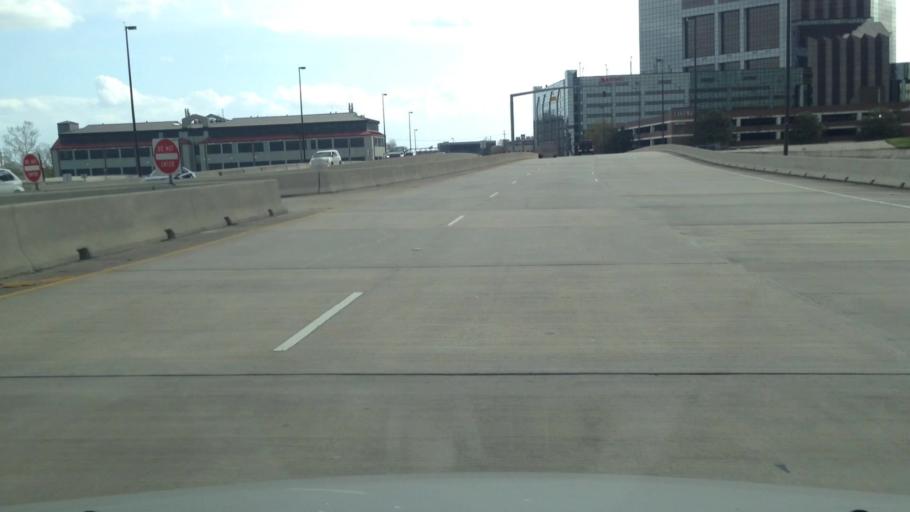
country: US
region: Louisiana
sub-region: Jefferson Parish
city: Metairie
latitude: 30.0212
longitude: -90.1542
